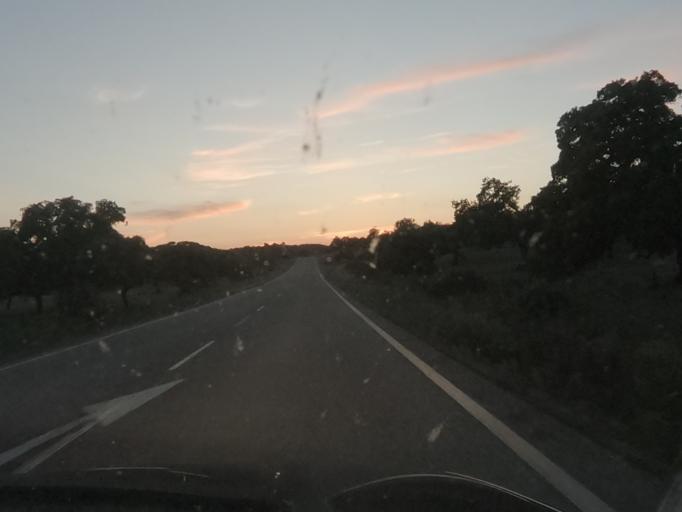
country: ES
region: Extremadura
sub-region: Provincia de Caceres
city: Piedras Albas
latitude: 39.7874
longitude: -6.9518
